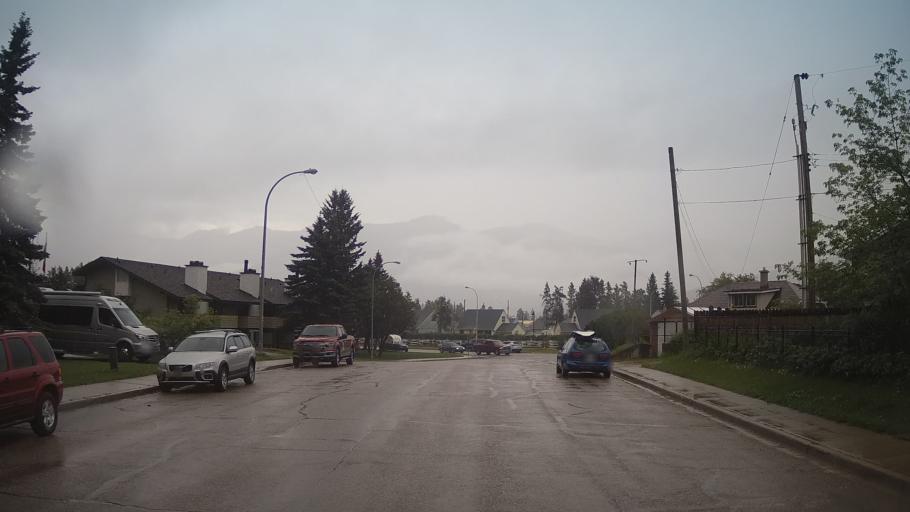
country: CA
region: Alberta
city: Jasper Park Lodge
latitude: 52.8838
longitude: -118.0822
